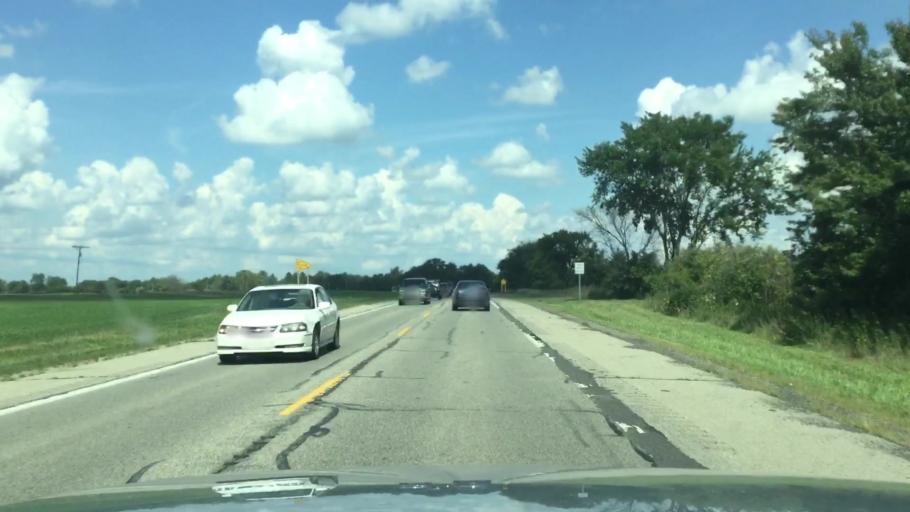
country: US
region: Michigan
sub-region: Lenawee County
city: Clinton
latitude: 42.1026
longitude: -83.8979
